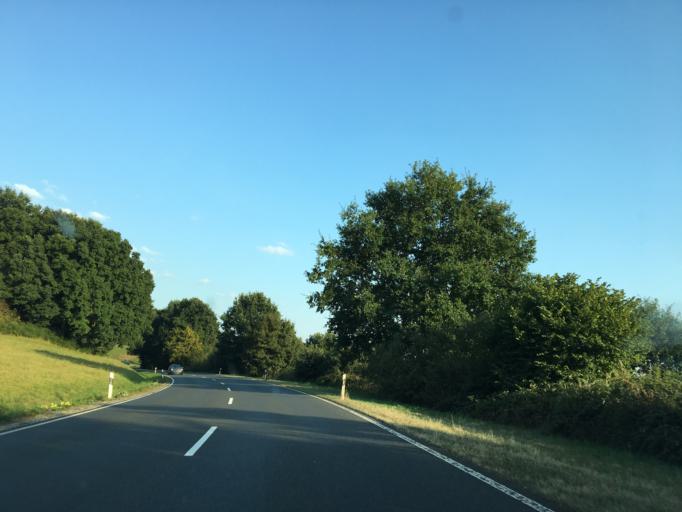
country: DE
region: Hesse
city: Wetter
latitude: 50.9174
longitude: 8.7093
